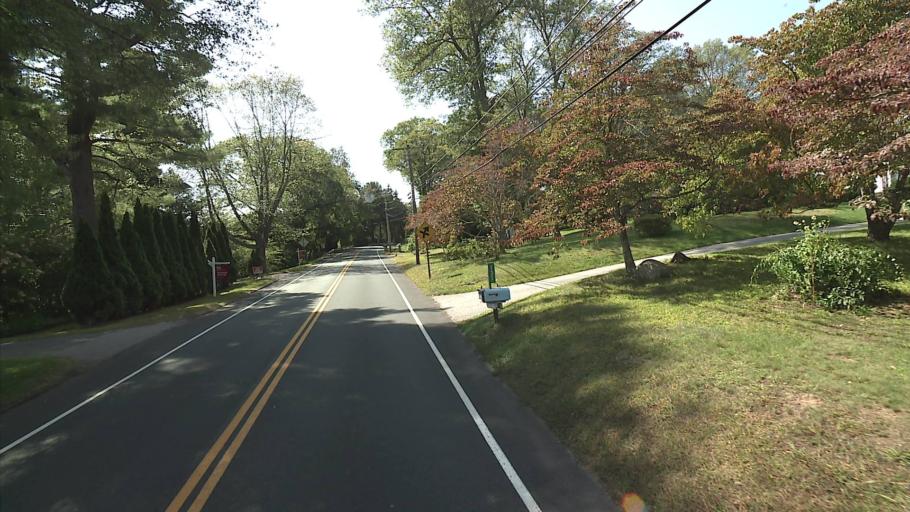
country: US
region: Connecticut
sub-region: Tolland County
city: Coventry Lake
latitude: 41.7170
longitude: -72.3243
